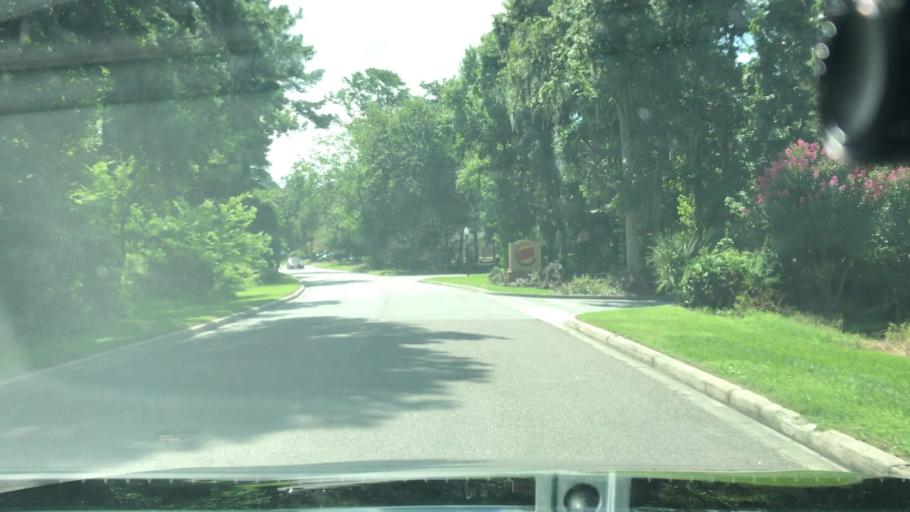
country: US
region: South Carolina
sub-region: Beaufort County
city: Hilton Head Island
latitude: 32.2148
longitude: -80.7295
